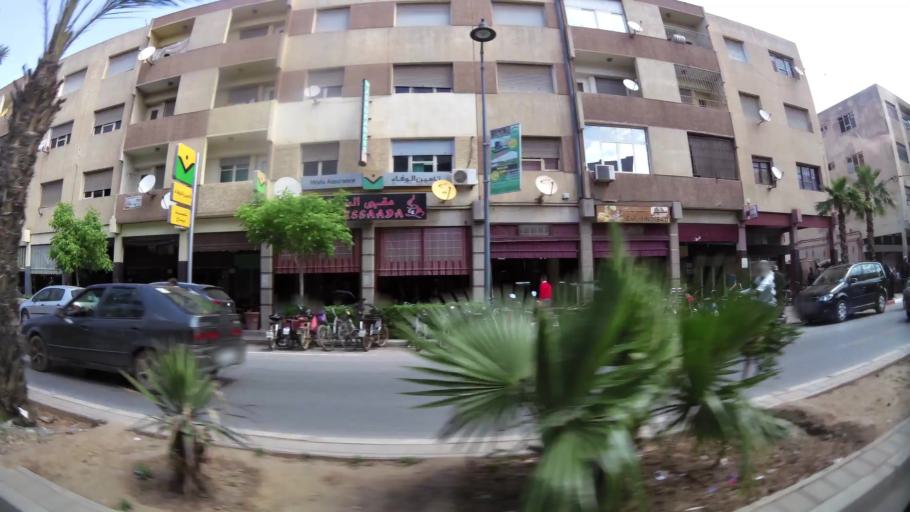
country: MA
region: Oriental
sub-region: Oujda-Angad
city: Oujda
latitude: 34.6799
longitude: -1.9040
